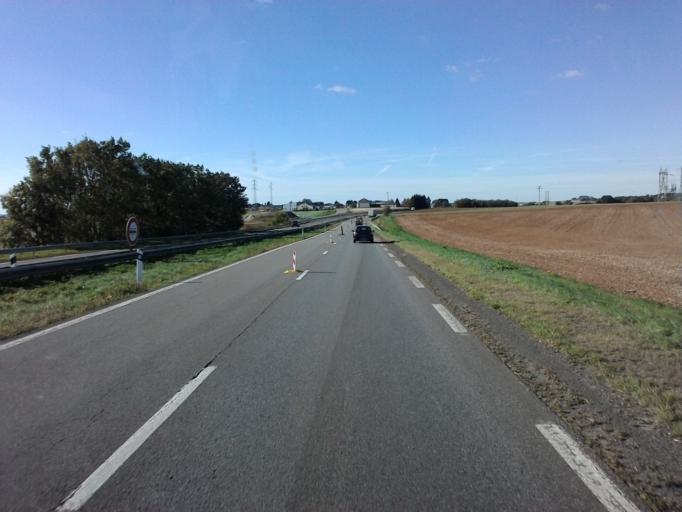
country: FR
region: Lorraine
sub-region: Departement de Meurthe-et-Moselle
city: Villers-la-Montagne
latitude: 49.4813
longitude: 5.8190
